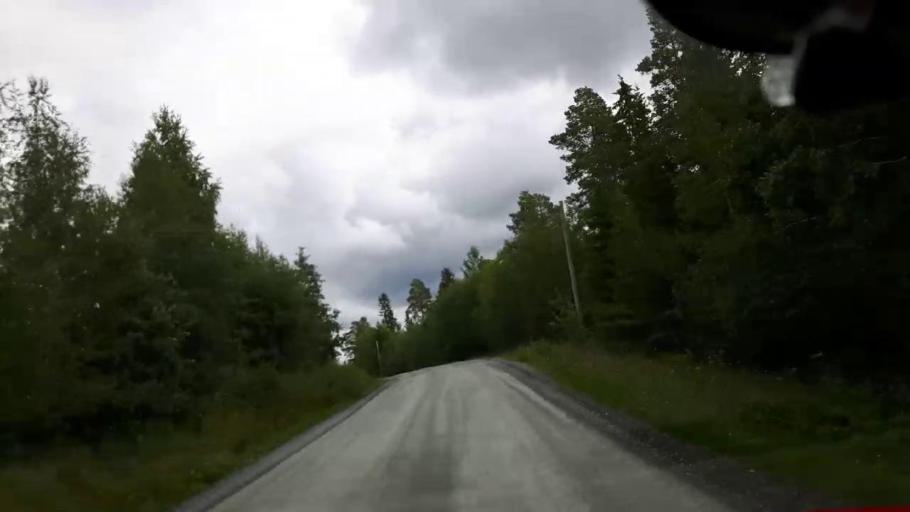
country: SE
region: Jaemtland
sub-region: Krokoms Kommun
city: Krokom
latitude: 63.5789
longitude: 14.2150
